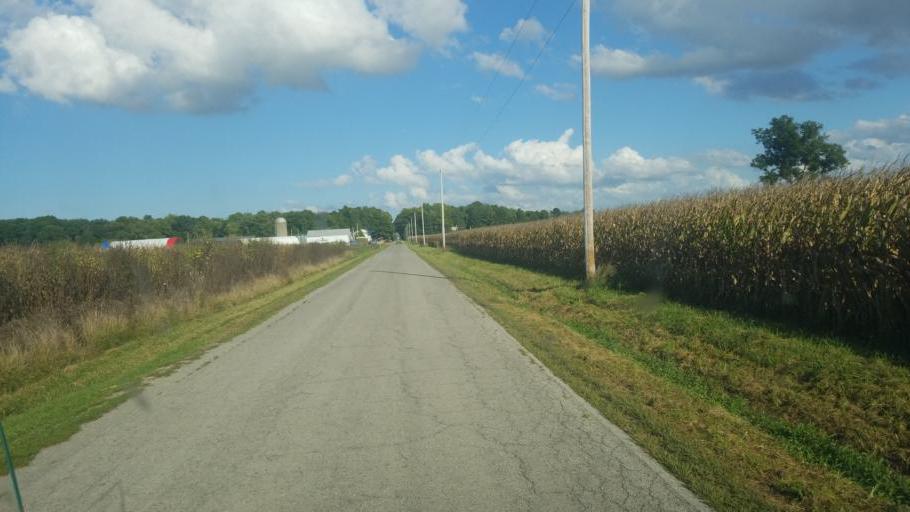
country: US
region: Ohio
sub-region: Hancock County
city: Arlington
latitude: 40.9360
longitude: -83.6856
